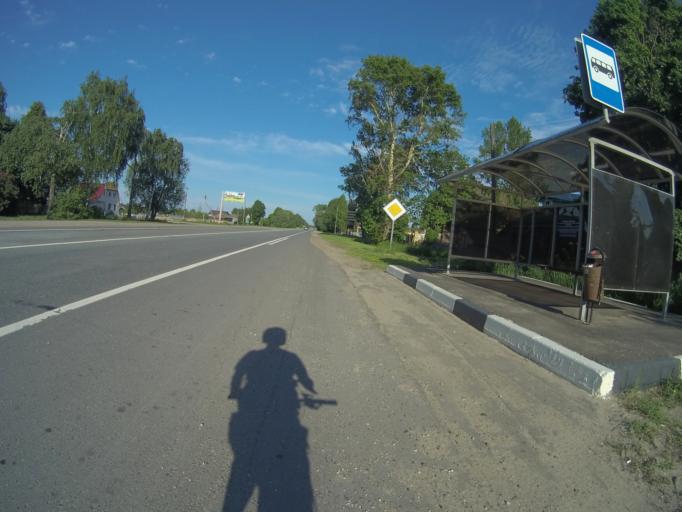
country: RU
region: Vladimir
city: Orgtrud
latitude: 56.1984
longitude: 40.8417
